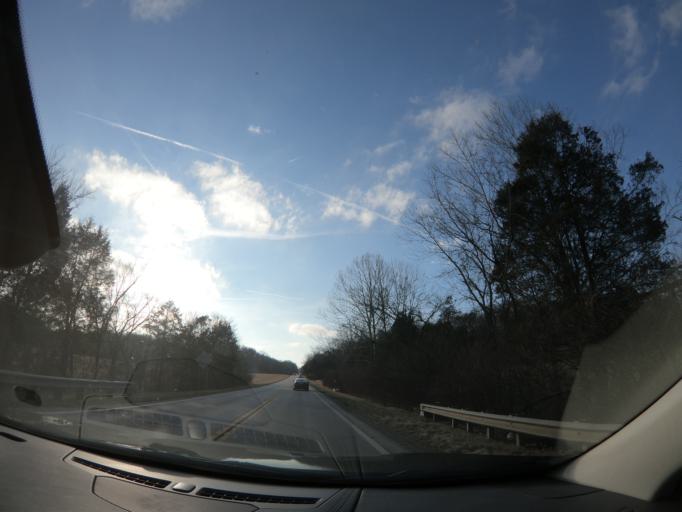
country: US
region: Kentucky
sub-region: Jefferson County
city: Middletown
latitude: 38.1908
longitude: -85.4882
